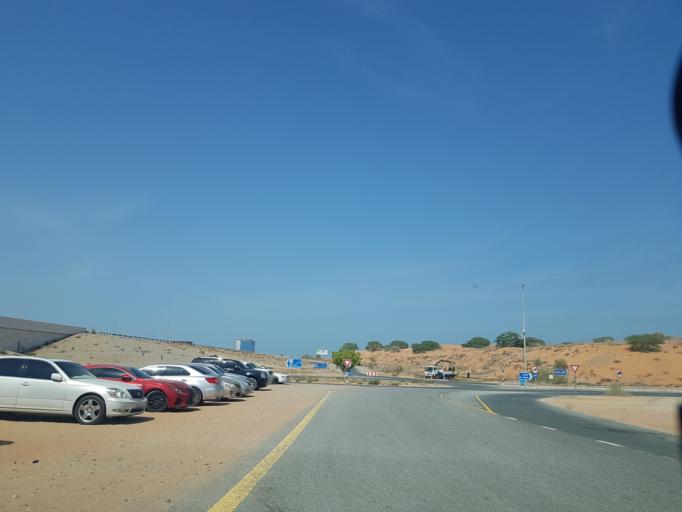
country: AE
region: Ra's al Khaymah
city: Ras al-Khaimah
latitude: 25.6991
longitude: 55.8749
